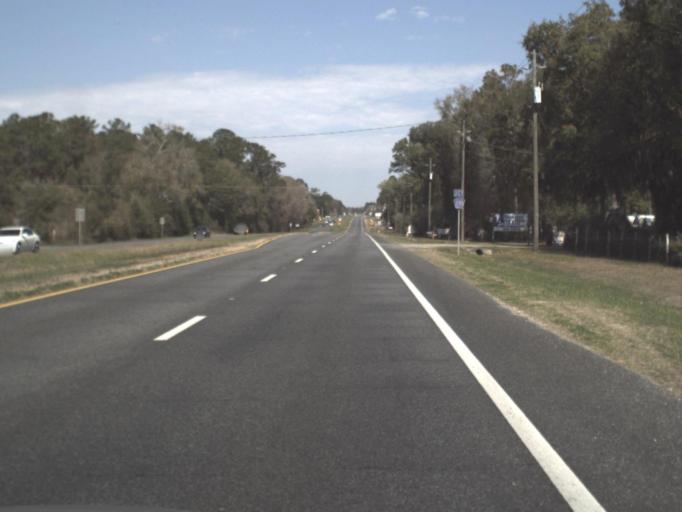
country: US
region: Florida
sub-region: Gadsden County
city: Havana
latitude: 30.5660
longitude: -84.3915
